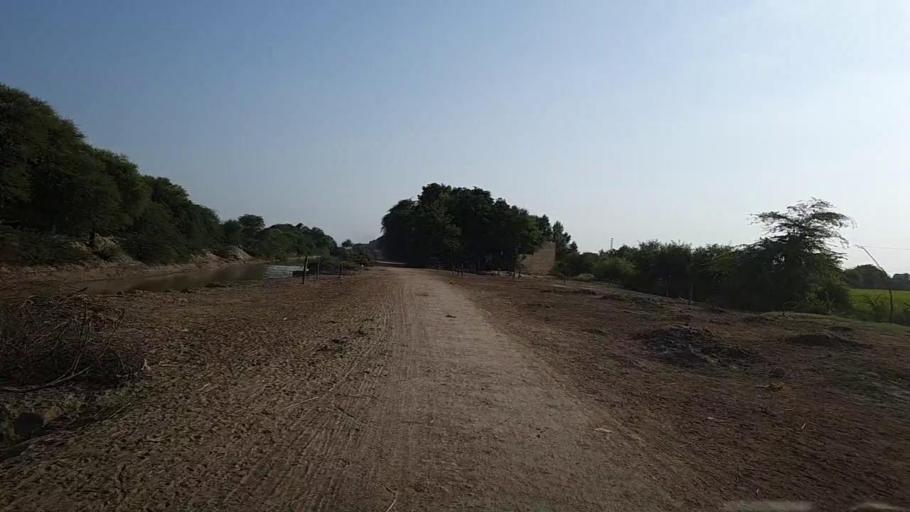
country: PK
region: Sindh
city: Kario
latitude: 24.7839
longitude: 68.6688
